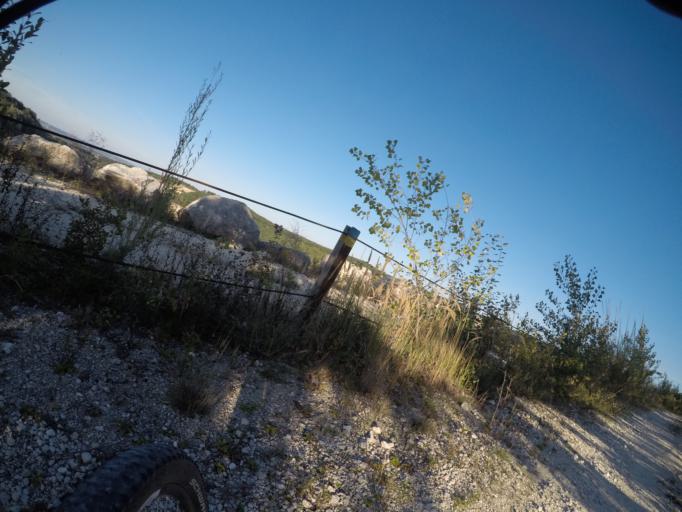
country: AT
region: Lower Austria
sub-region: Politischer Bezirk Bruck an der Leitha
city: Mannersdorf am Leithagebirge
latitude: 47.9608
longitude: 16.6015
